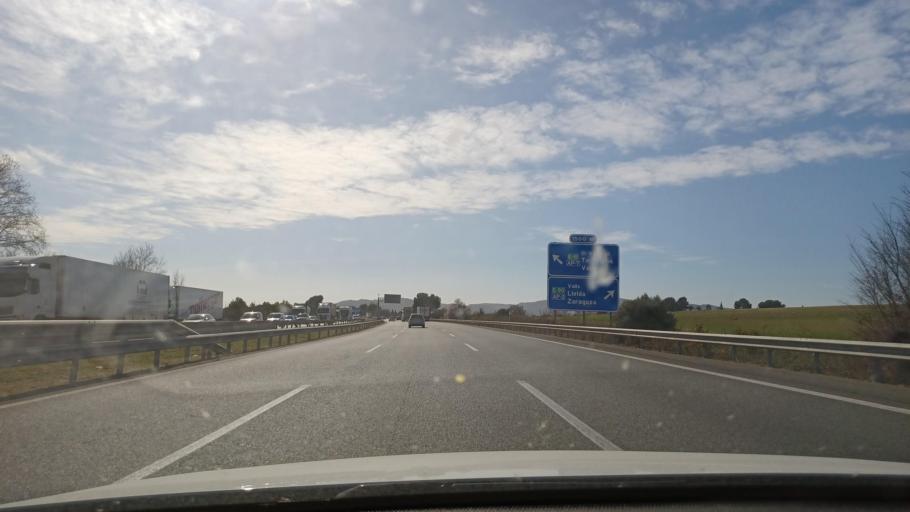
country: ES
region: Catalonia
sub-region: Provincia de Tarragona
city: Sant Jaume dels Domenys
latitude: 41.2777
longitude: 1.5625
